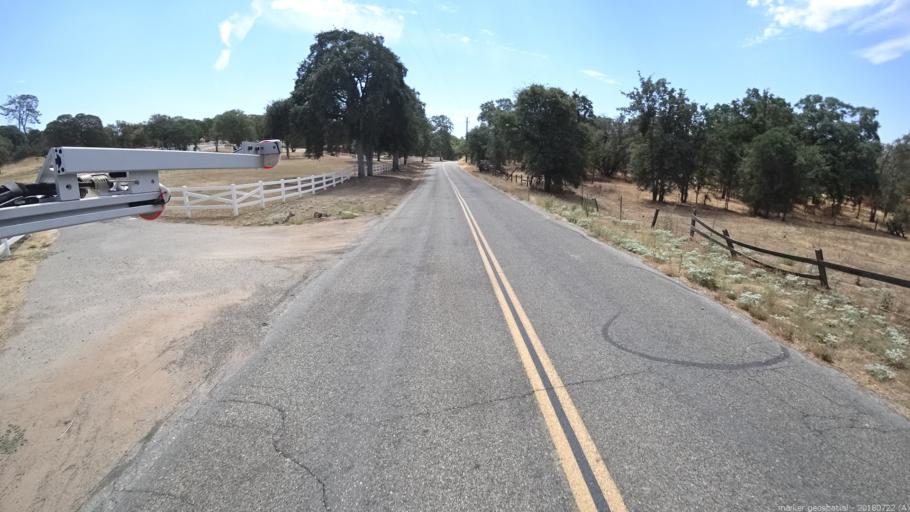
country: US
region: California
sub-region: Madera County
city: Coarsegold
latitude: 37.2709
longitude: -119.7386
